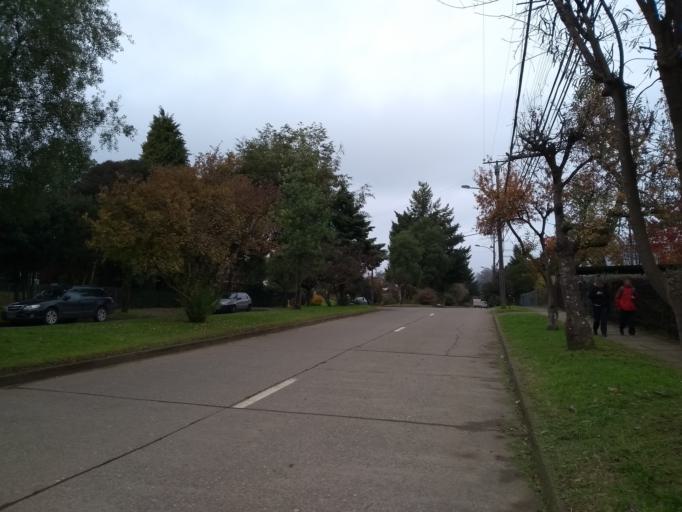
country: CL
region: Los Rios
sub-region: Provincia de Valdivia
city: Valdivia
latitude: -39.8088
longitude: -73.2628
